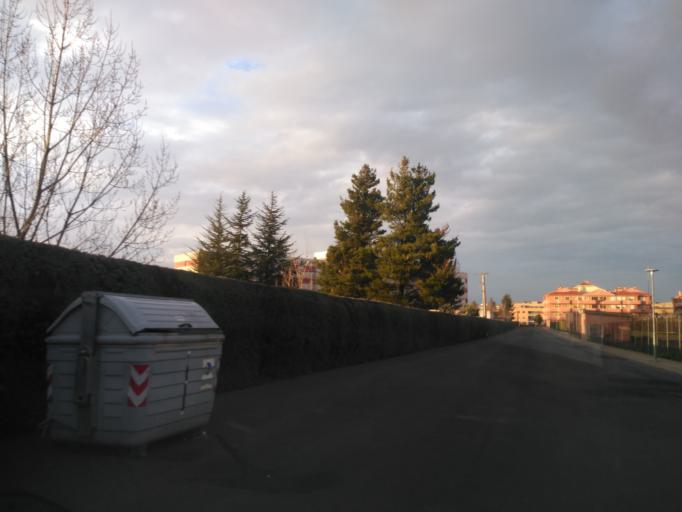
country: ES
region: Castille and Leon
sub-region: Provincia de Salamanca
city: Santa Marta de Tormes
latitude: 40.9479
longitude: -5.6389
